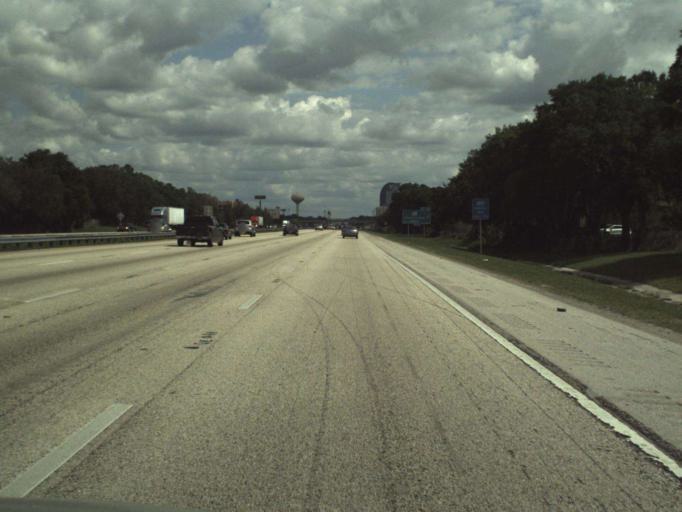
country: US
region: Florida
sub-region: Seminole County
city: Altamonte Springs
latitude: 28.6526
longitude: -81.3883
